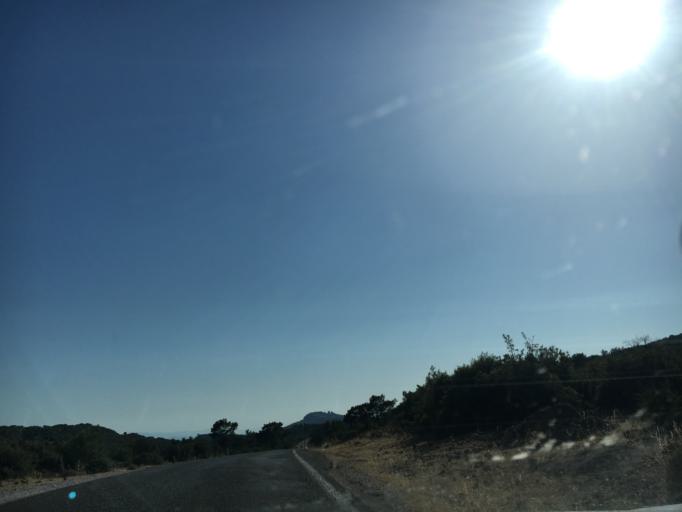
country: TR
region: Canakkale
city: Behram
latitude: 39.5096
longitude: 26.3807
